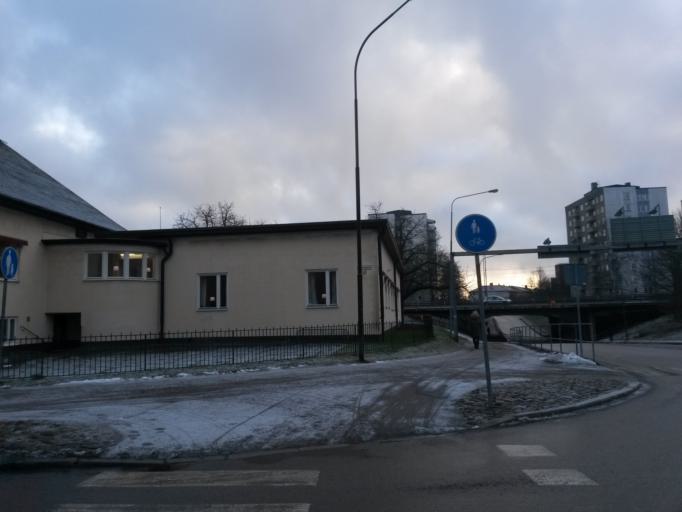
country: SE
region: Vaermland
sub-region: Karlstads Kommun
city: Karlstad
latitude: 59.3794
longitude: 13.4909
